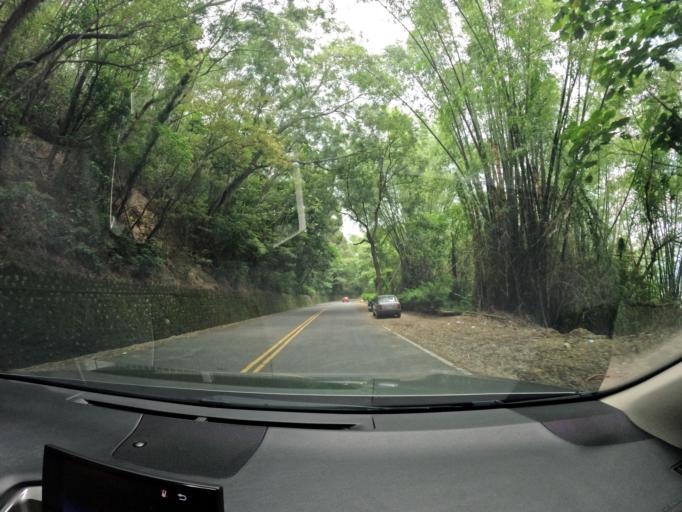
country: TW
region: Taiwan
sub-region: Nantou
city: Nantou
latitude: 23.8883
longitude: 120.6295
